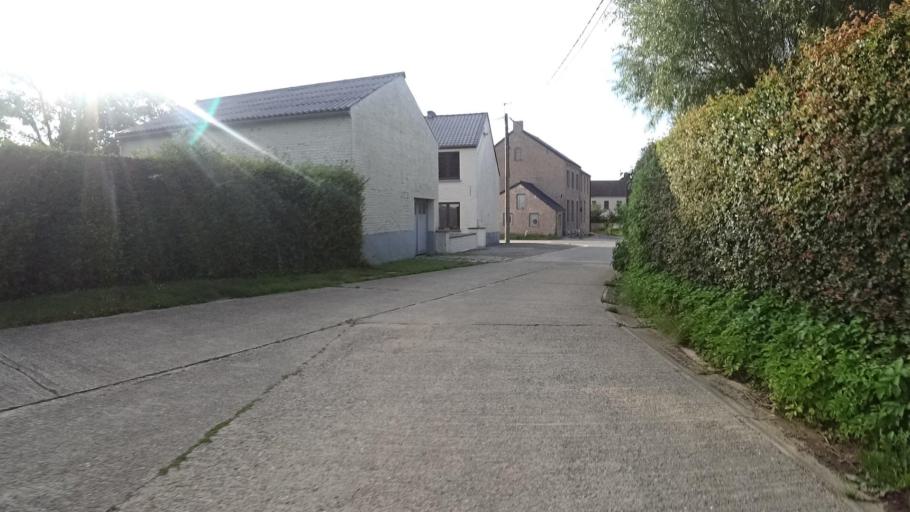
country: BE
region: Wallonia
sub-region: Province du Brabant Wallon
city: Walhain-Saint-Paul
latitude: 50.6404
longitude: 4.6806
